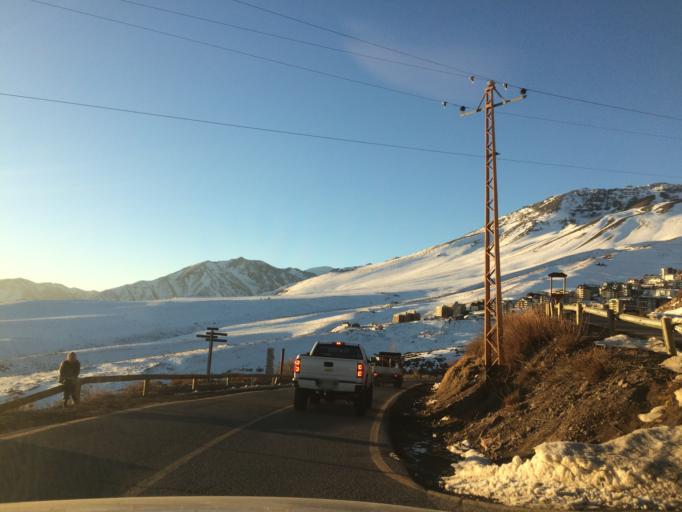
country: CL
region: Santiago Metropolitan
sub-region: Provincia de Santiago
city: Villa Presidente Frei, Nunoa, Santiago, Chile
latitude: -33.3432
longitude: -70.2948
